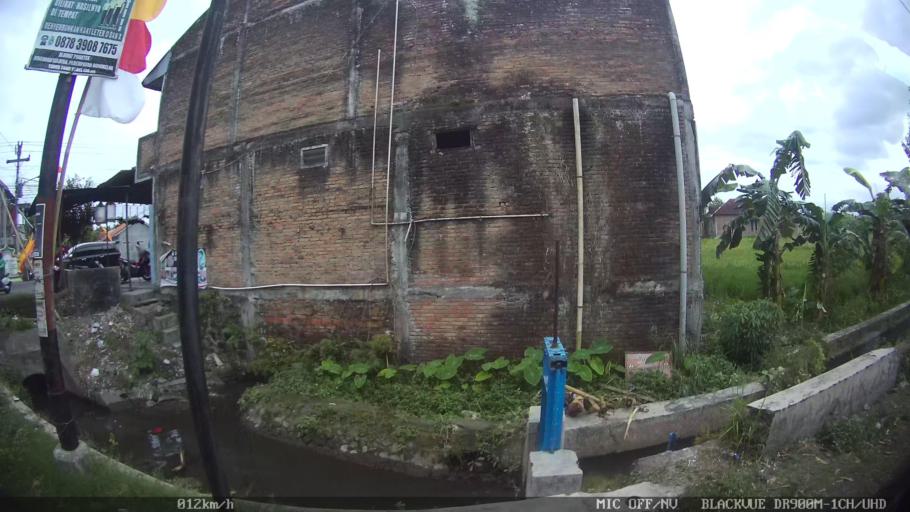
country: ID
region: Daerah Istimewa Yogyakarta
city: Sewon
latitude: -7.8384
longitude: 110.4121
